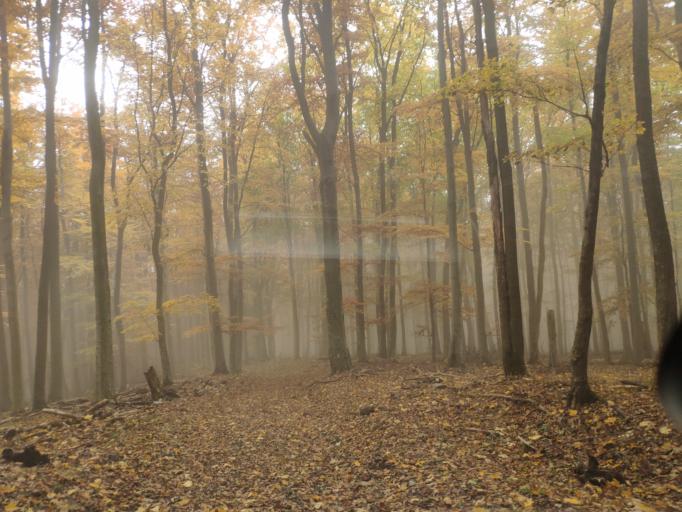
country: SK
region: Kosicky
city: Moldava nad Bodvou
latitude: 48.7309
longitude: 21.0137
